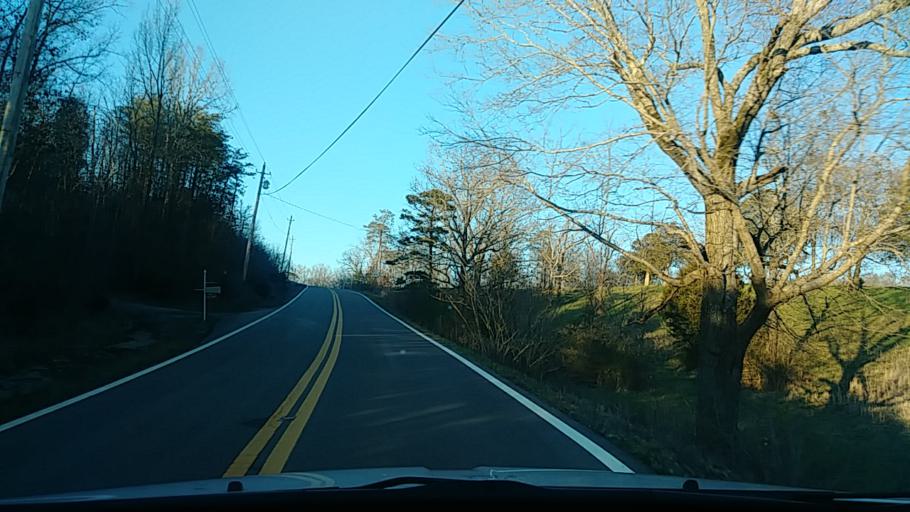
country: US
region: Tennessee
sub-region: Greene County
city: Mosheim
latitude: 36.1141
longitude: -83.0768
